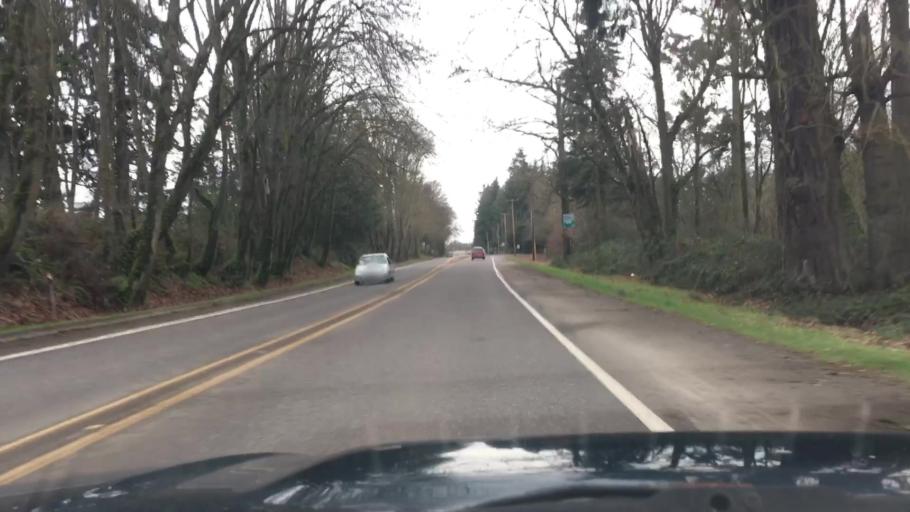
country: US
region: Oregon
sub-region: Lane County
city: Coburg
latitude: 44.1094
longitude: -123.0503
